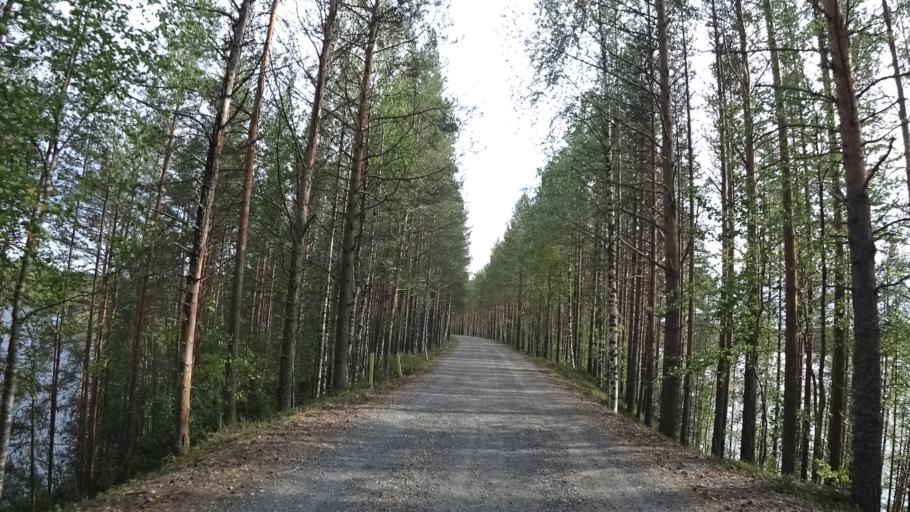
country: FI
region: North Karelia
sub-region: Joensuu
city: Ilomantsi
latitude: 62.6202
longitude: 31.1937
